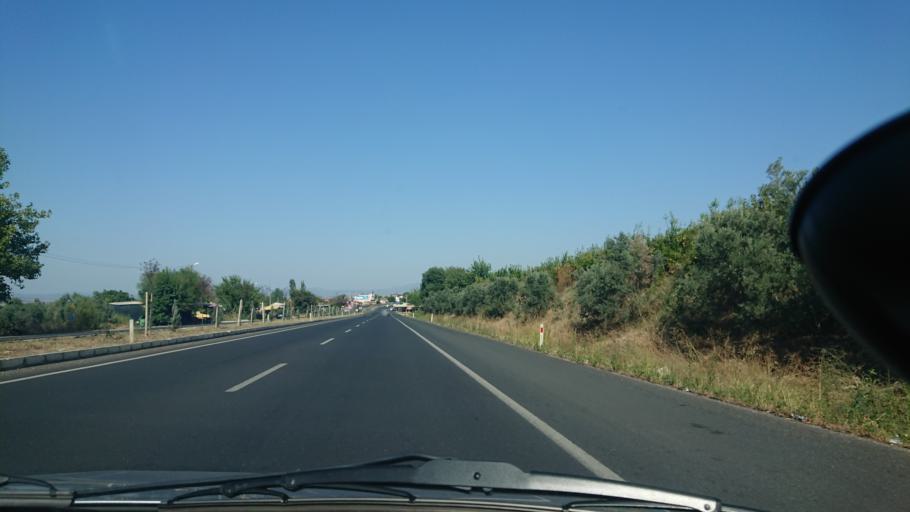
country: TR
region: Manisa
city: Ahmetli
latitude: 38.4874
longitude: 27.8329
